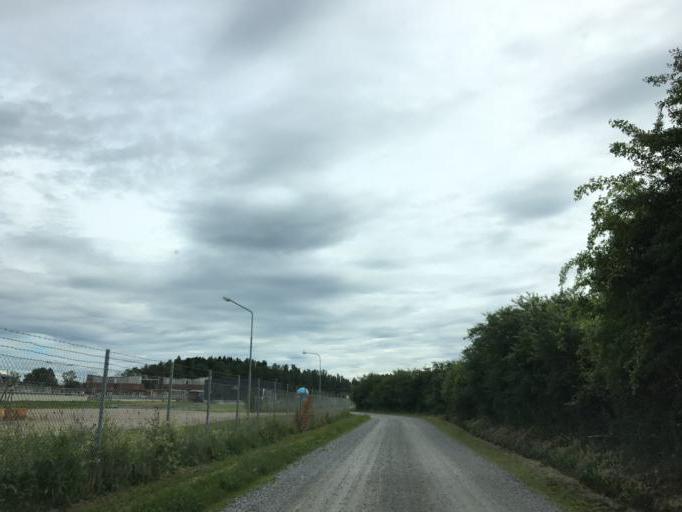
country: SE
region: Soedermanland
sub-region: Eskilstuna Kommun
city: Torshalla
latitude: 59.3878
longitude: 16.4584
